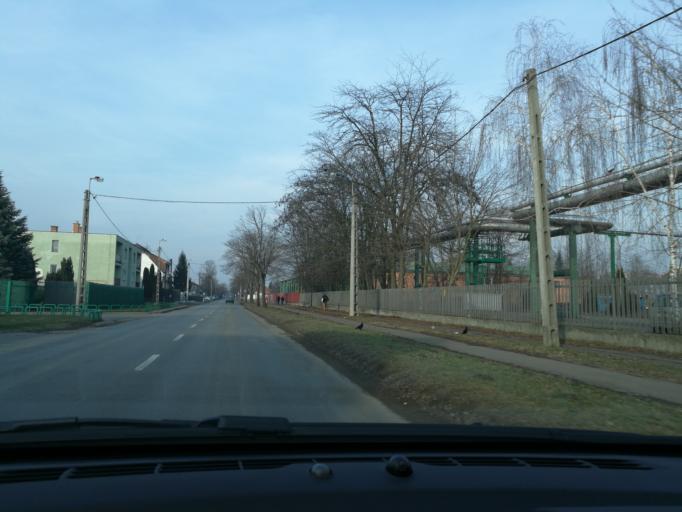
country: HU
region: Szabolcs-Szatmar-Bereg
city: Nyiregyhaza
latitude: 47.9476
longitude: 21.6945
